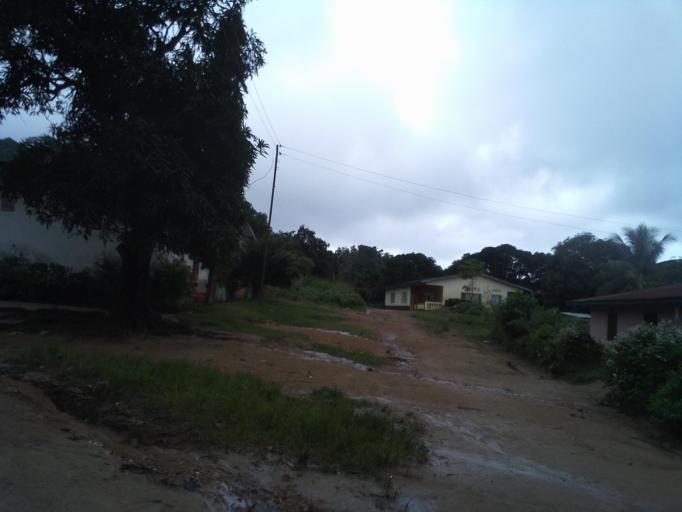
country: SL
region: Eastern Province
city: Kenema
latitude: 7.8540
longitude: -11.2121
